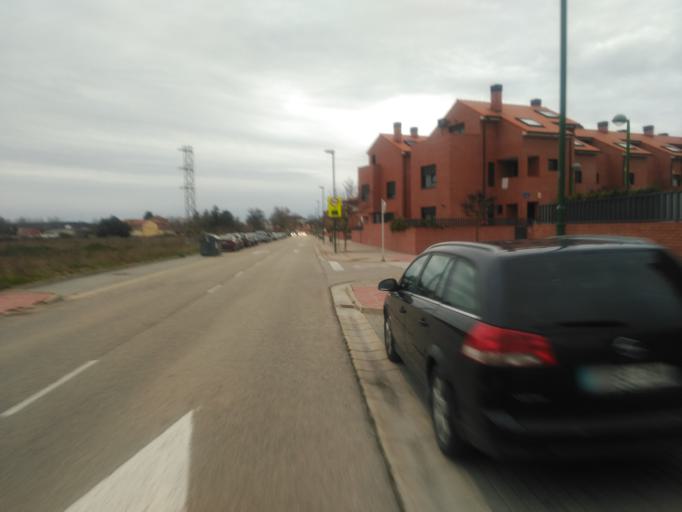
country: ES
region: Castille and Leon
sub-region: Provincia de Burgos
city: Villagonzalo-Pedernales
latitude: 42.3407
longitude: -3.7347
